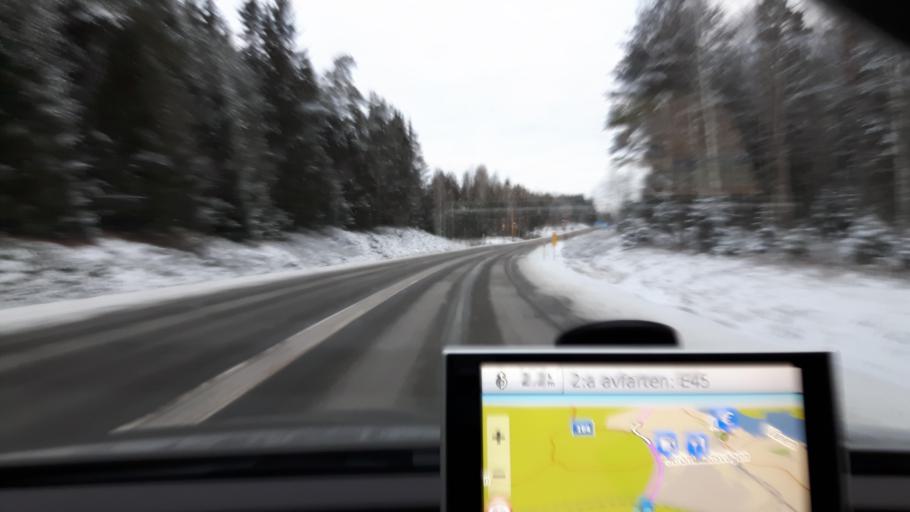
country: SE
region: Vaestra Goetaland
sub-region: Amals Kommun
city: Amal
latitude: 59.0360
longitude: 12.6711
